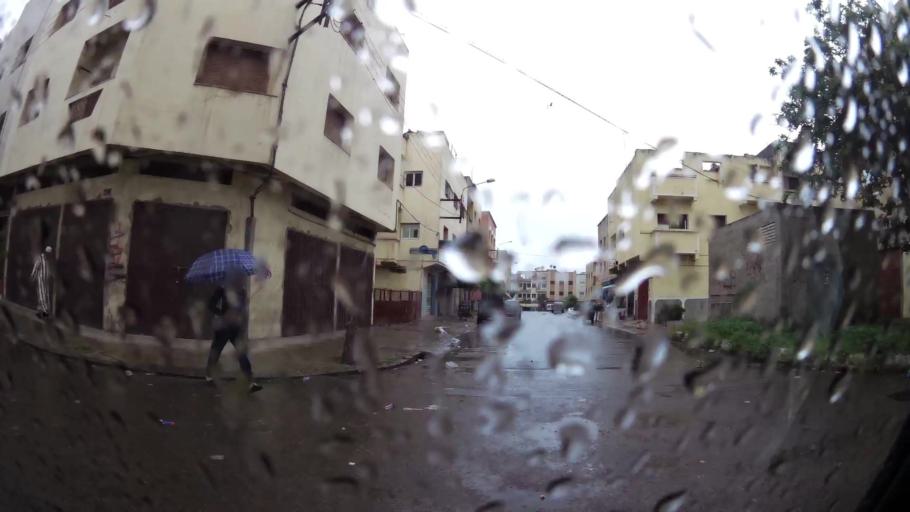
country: MA
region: Grand Casablanca
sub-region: Casablanca
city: Casablanca
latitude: 33.5503
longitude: -7.6817
